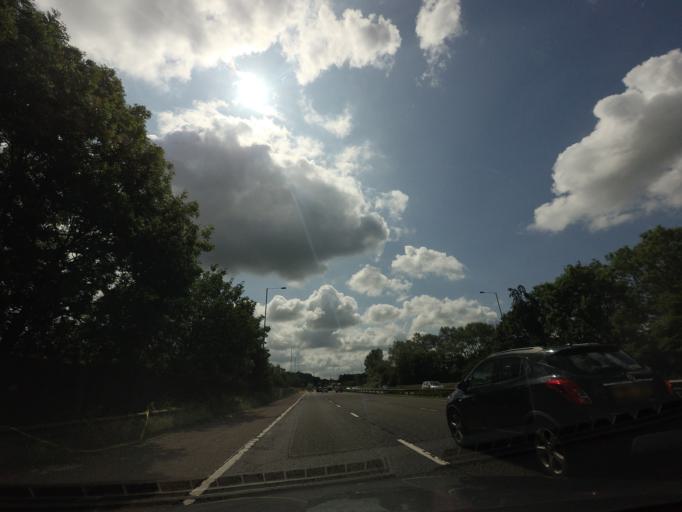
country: GB
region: England
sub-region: Lancashire
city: Euxton
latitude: 53.6558
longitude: -2.6910
